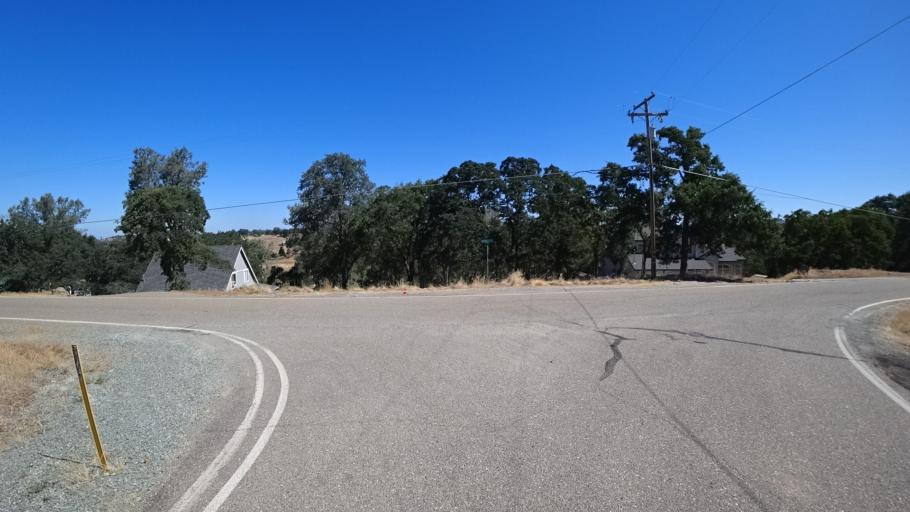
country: US
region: California
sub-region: Calaveras County
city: Rancho Calaveras
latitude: 38.1082
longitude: -120.8700
